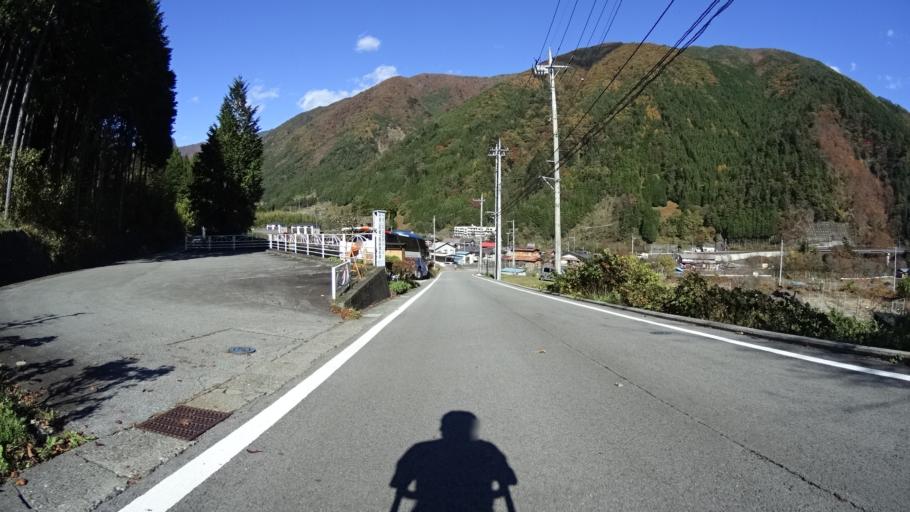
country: JP
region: Yamanashi
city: Otsuki
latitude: 35.7898
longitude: 138.9208
